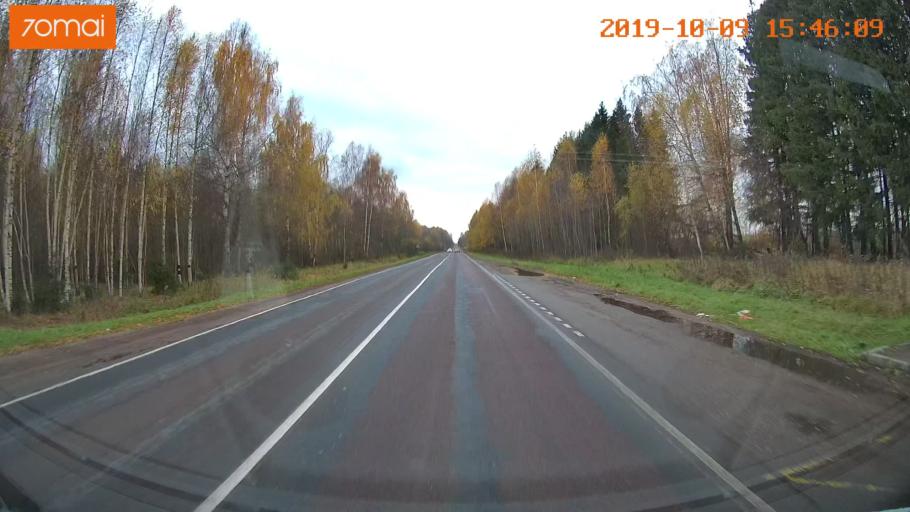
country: RU
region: Kostroma
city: Oktyabr'skiy
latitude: 57.8272
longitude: 41.0492
